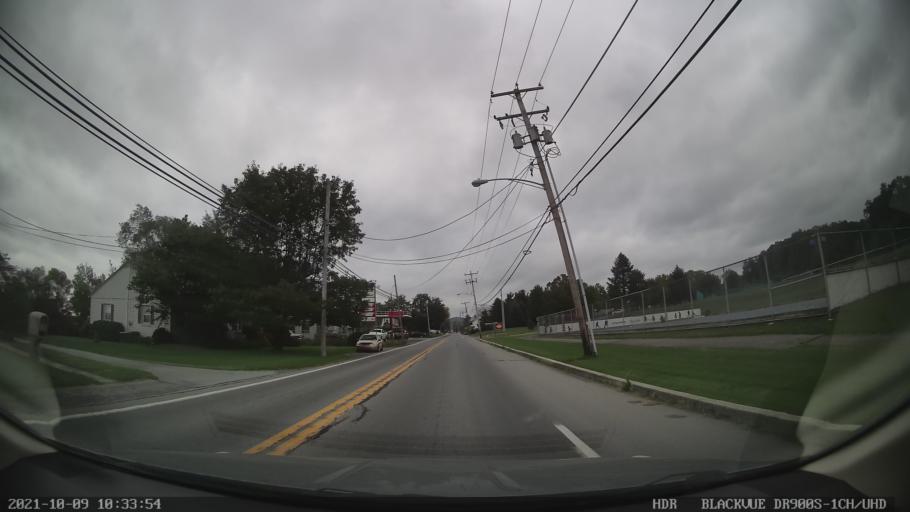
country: US
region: Pennsylvania
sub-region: Berks County
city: Topton
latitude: 40.5047
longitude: -75.6634
